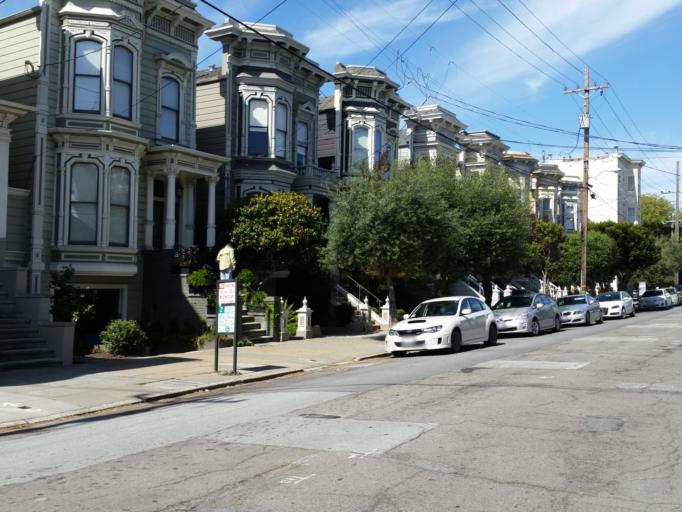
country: US
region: California
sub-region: San Francisco County
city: San Francisco
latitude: 37.7864
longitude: -122.4417
